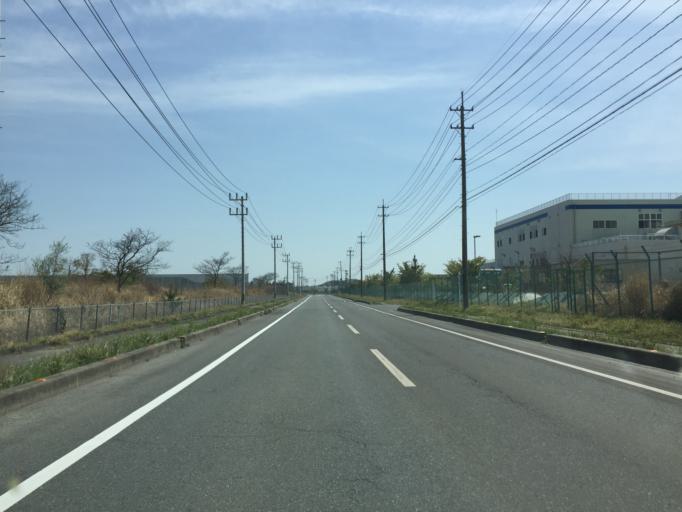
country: JP
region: Miyagi
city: Marumori
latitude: 37.8326
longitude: 140.9455
